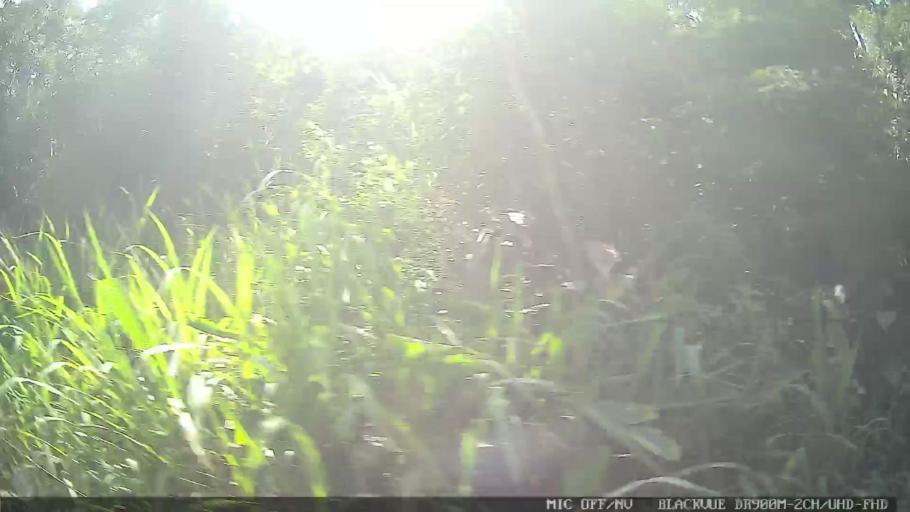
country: BR
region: Sao Paulo
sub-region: Santa Isabel
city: Santa Isabel
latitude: -23.3570
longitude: -46.1965
